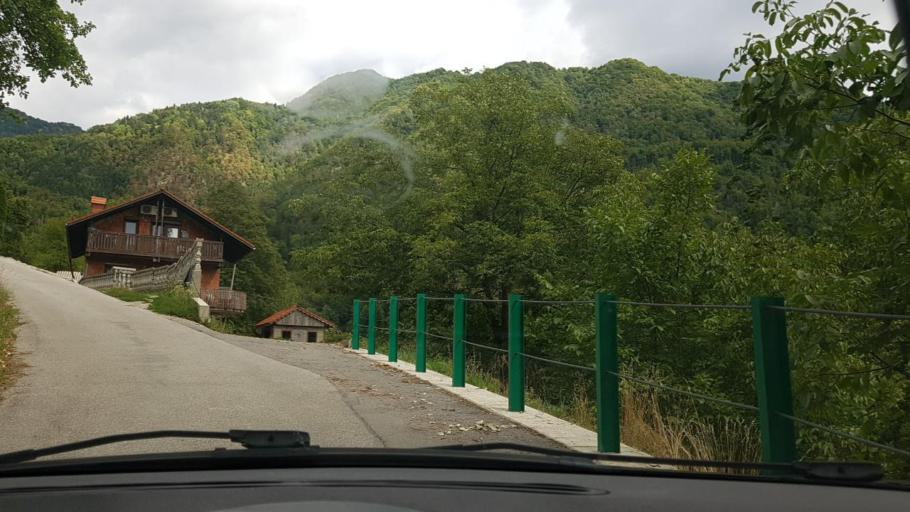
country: SI
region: Tolmin
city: Tolmin
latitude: 46.2025
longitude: 13.7476
